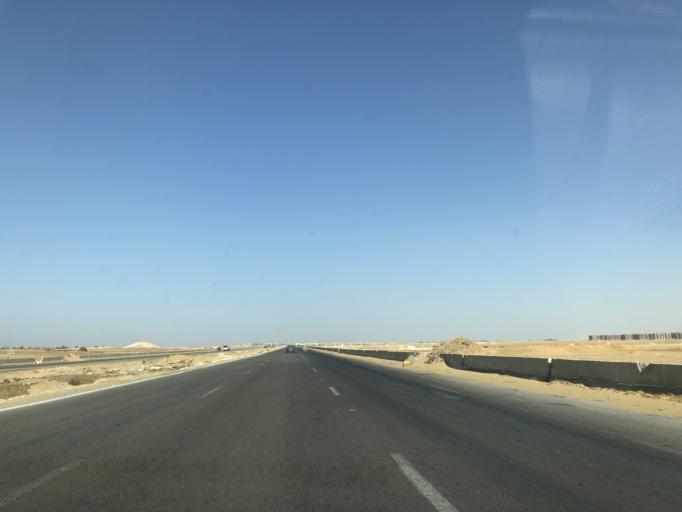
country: EG
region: Muhafazat al Minufiyah
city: Ashmun
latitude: 30.0678
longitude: 30.8779
